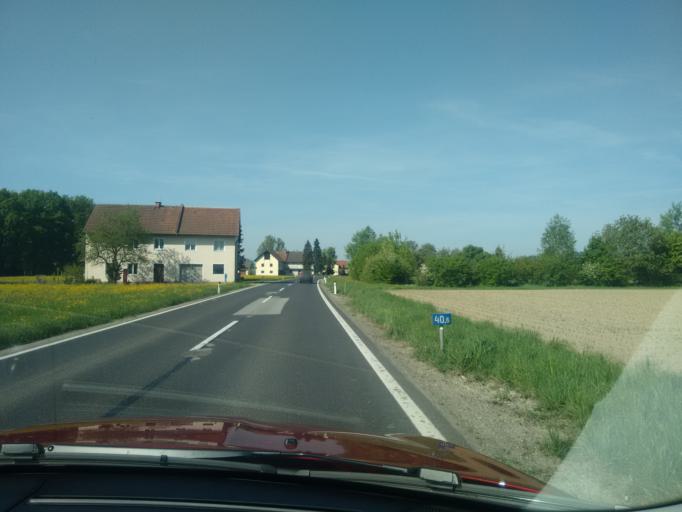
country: AT
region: Upper Austria
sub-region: Politischer Bezirk Grieskirchen
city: Grieskirchen
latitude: 48.3346
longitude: 13.8407
